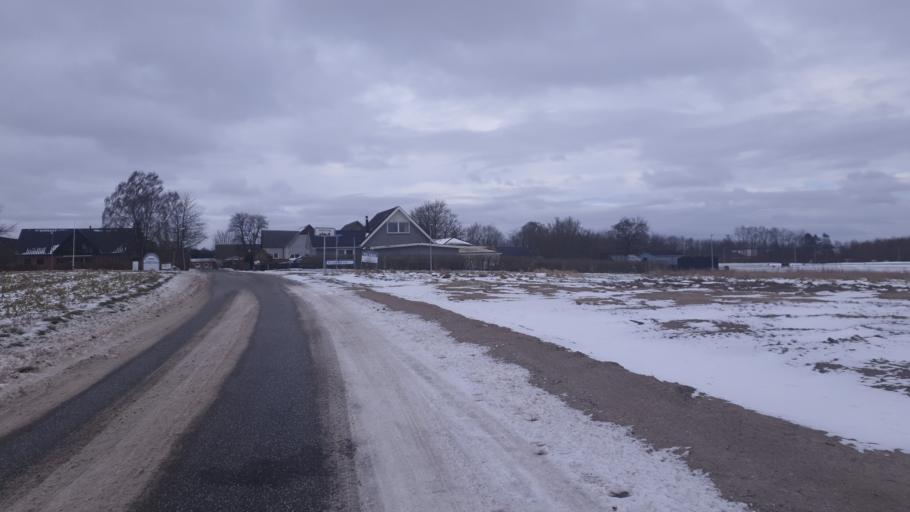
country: DK
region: Central Jutland
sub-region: Hedensted Kommune
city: Hedensted
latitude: 55.8009
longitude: 9.7058
